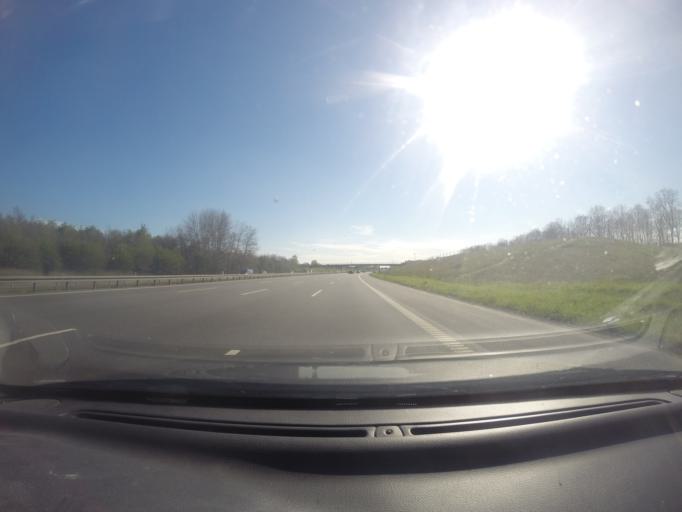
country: DK
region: Capital Region
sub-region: Ballerup Kommune
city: Ballerup
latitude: 55.6991
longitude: 12.3640
